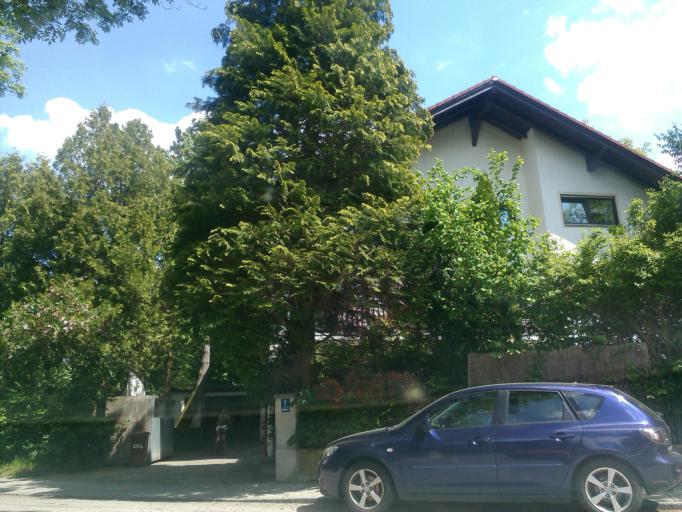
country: DE
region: Bavaria
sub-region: Upper Bavaria
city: Pullach im Isartal
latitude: 48.0783
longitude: 11.5151
